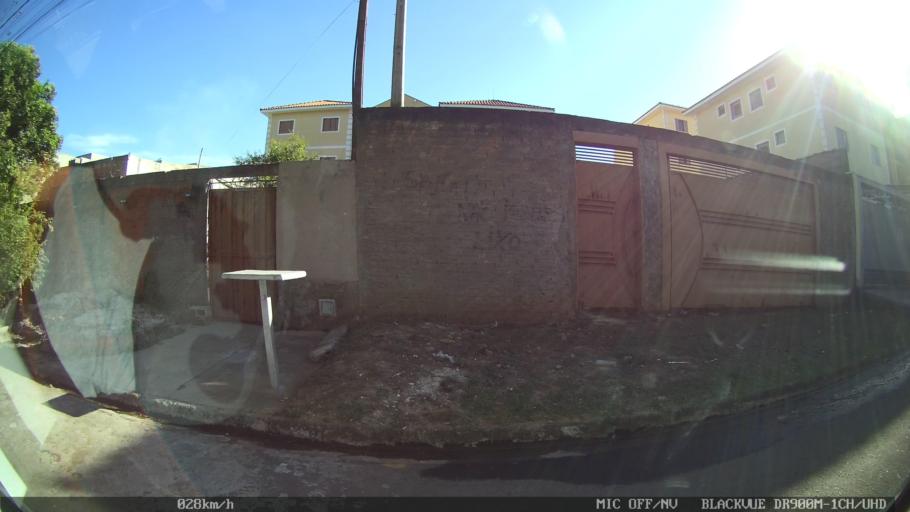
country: BR
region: Sao Paulo
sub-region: Franca
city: Franca
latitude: -20.4830
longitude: -47.4217
